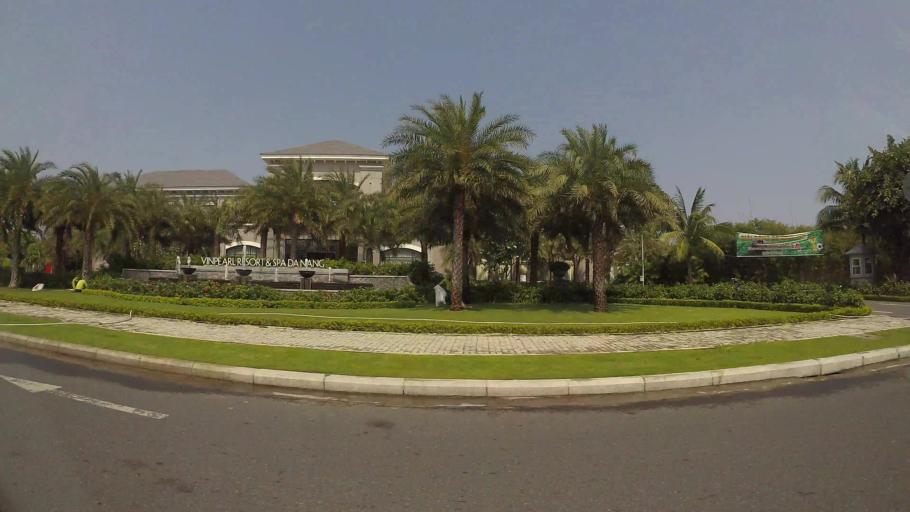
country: VN
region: Da Nang
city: Ngu Hanh Son
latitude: 15.9939
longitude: 108.2687
